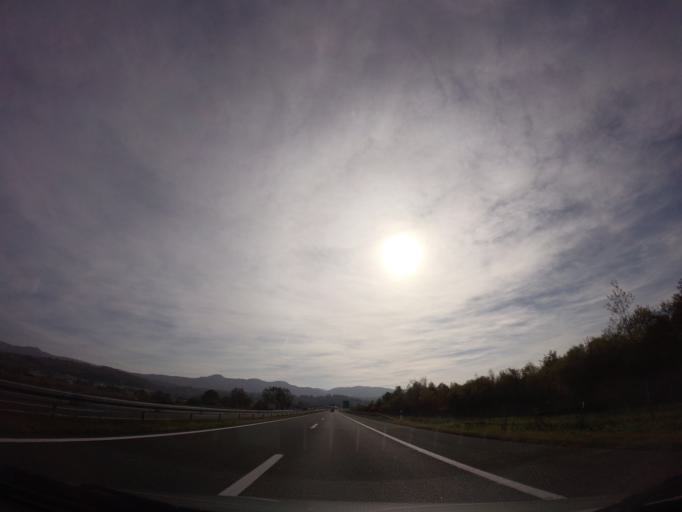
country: HR
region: Varazdinska
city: Ljubescica
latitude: 46.1644
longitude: 16.3751
